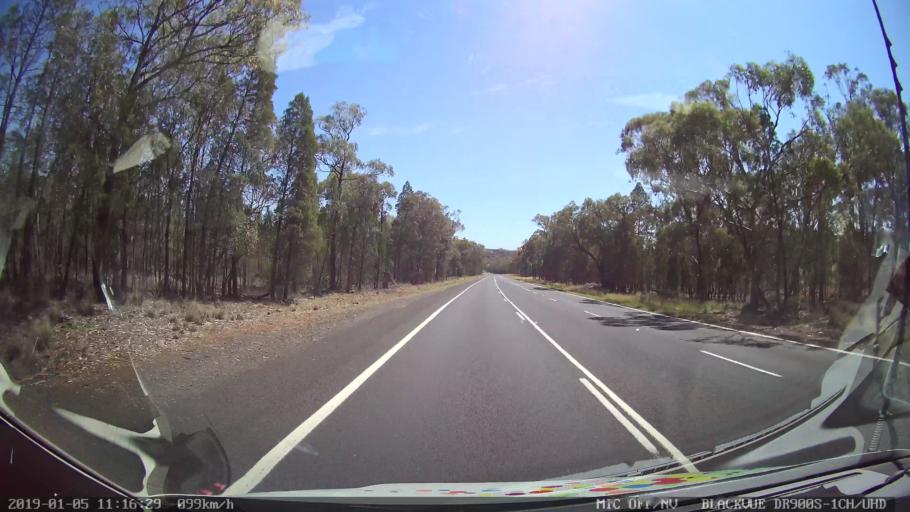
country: AU
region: New South Wales
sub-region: Warrumbungle Shire
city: Coonabarabran
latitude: -31.3382
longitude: 149.2985
